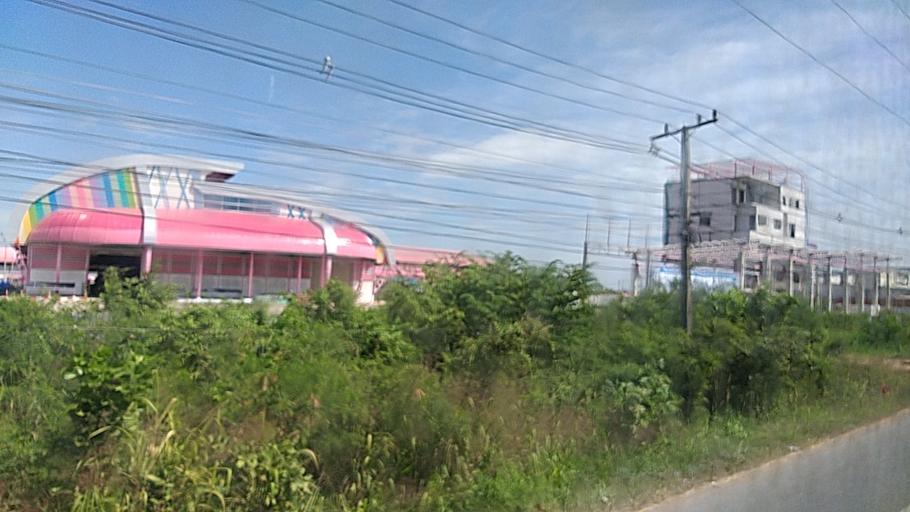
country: TH
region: Khon Kaen
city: Khon Kaen
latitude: 16.4377
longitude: 102.9231
